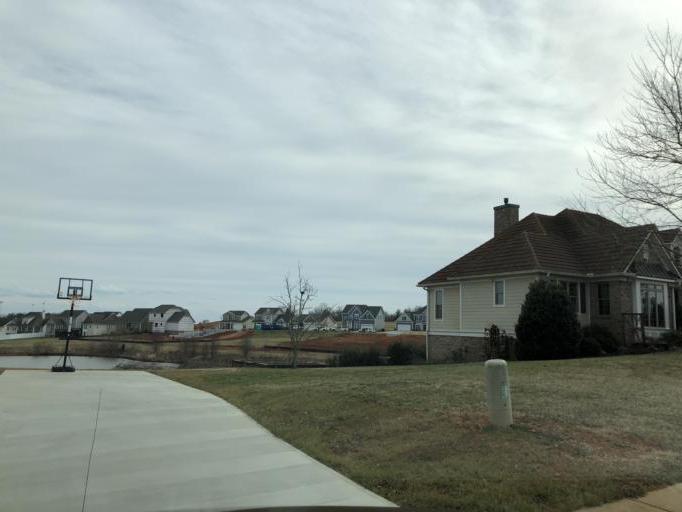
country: US
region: North Carolina
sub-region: Cleveland County
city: Shelby
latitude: 35.2585
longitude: -81.5011
